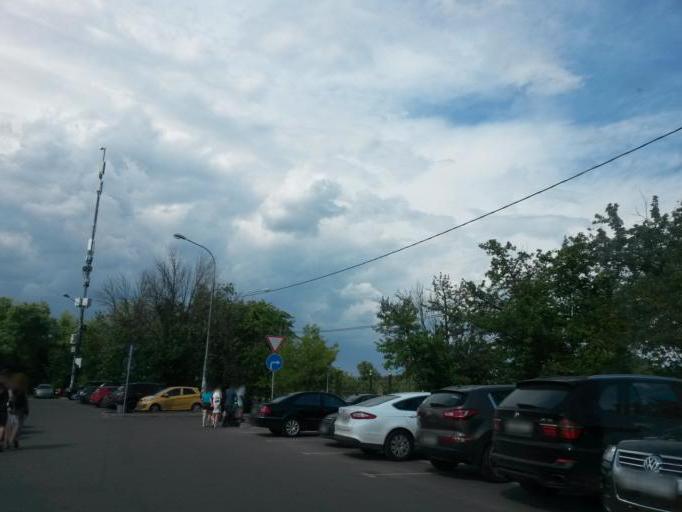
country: RU
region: Moscow
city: Orekhovo-Borisovo Severnoye
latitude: 55.6148
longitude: 37.6741
